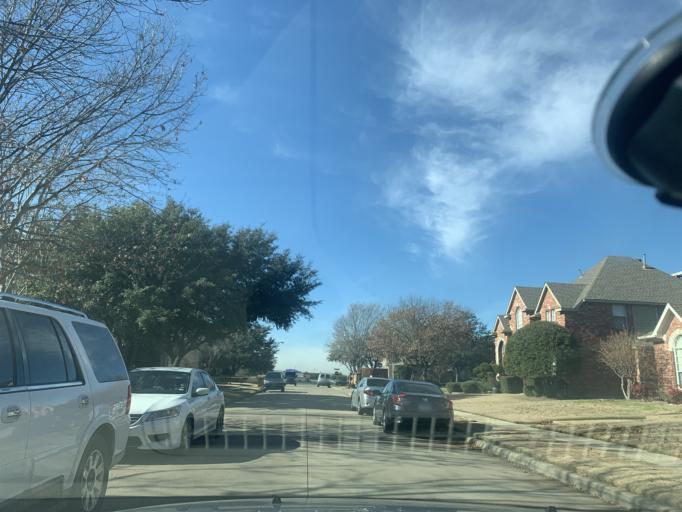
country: US
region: Texas
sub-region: Denton County
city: The Colony
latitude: 33.0520
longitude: -96.8250
